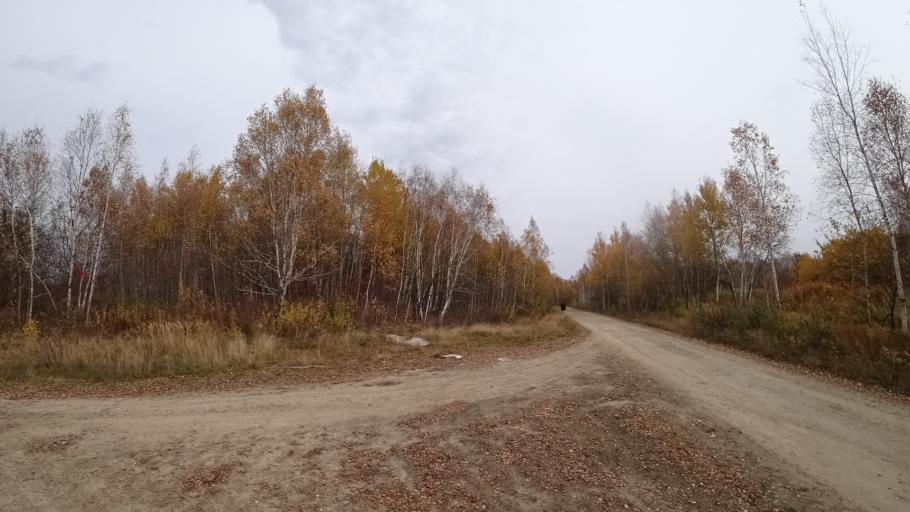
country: RU
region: Khabarovsk Krai
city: Amursk
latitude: 50.1491
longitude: 136.9820
